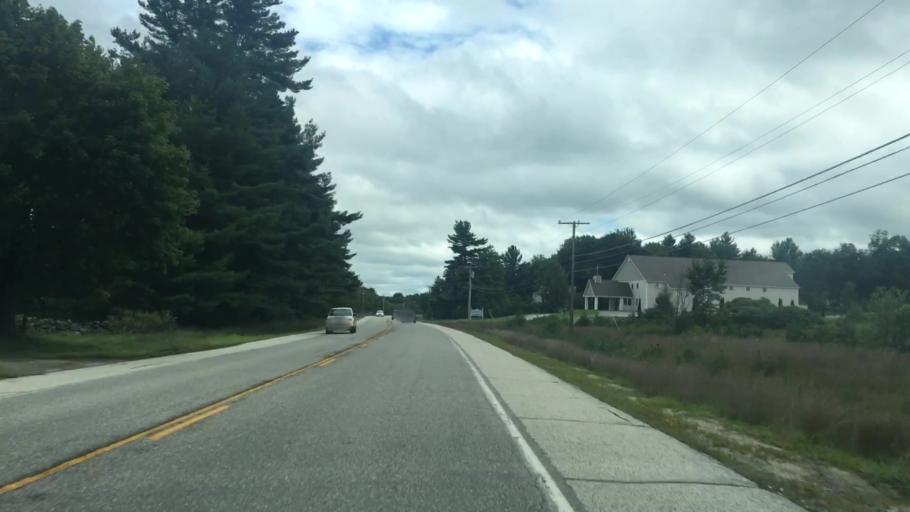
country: US
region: Maine
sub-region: York County
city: Lake Arrowhead
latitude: 43.6378
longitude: -70.7504
